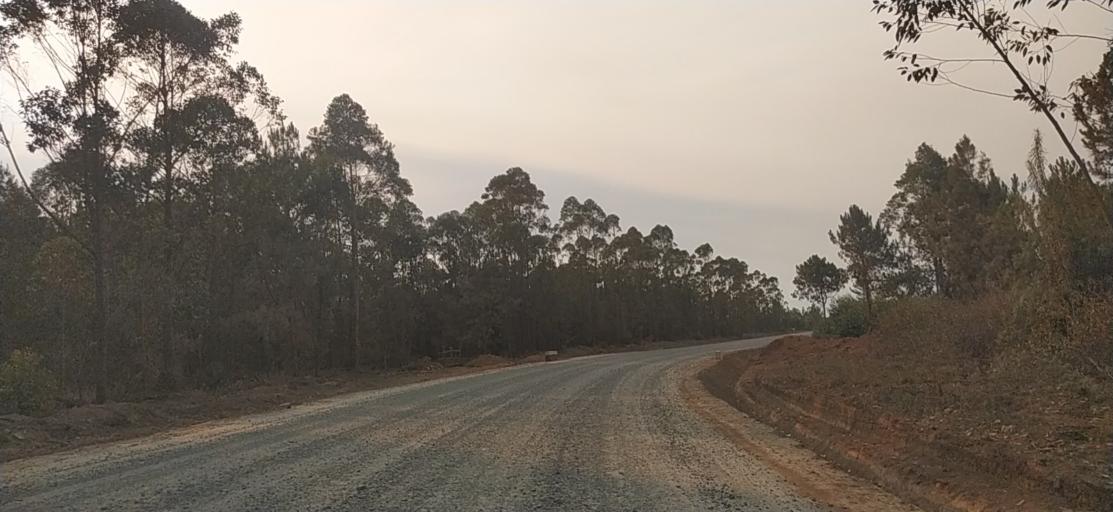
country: MG
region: Alaotra Mangoro
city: Moramanga
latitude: -18.5601
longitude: 48.2599
